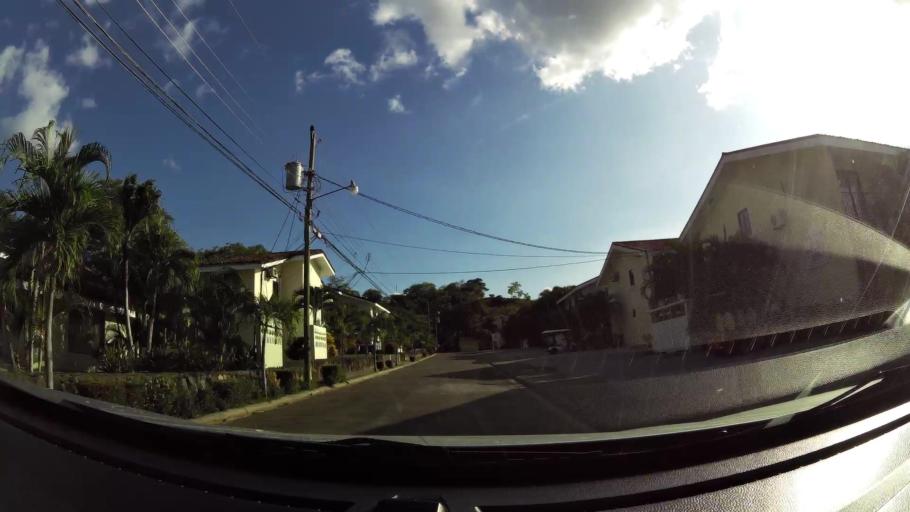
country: CR
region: Guanacaste
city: Sardinal
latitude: 10.5524
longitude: -85.6907
